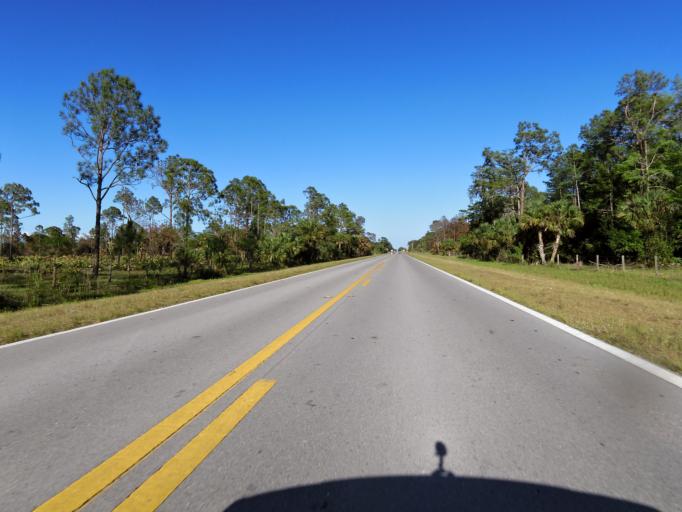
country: US
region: Florida
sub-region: Collier County
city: Immokalee
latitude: 26.3031
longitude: -81.3500
